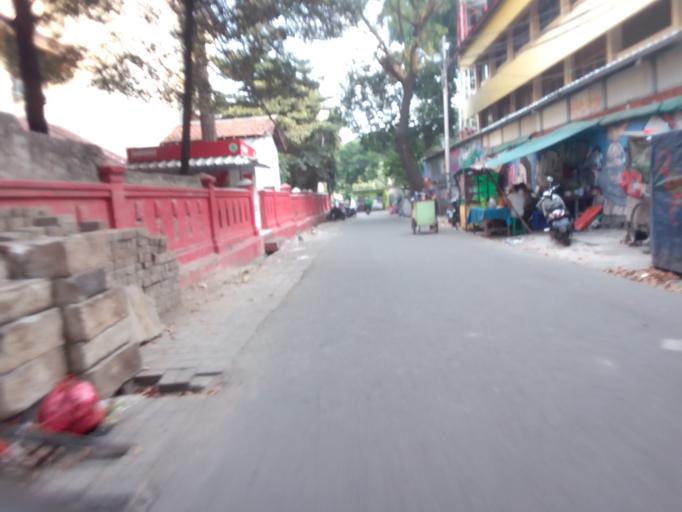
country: ID
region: Jakarta Raya
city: Jakarta
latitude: -6.1996
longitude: 106.8141
